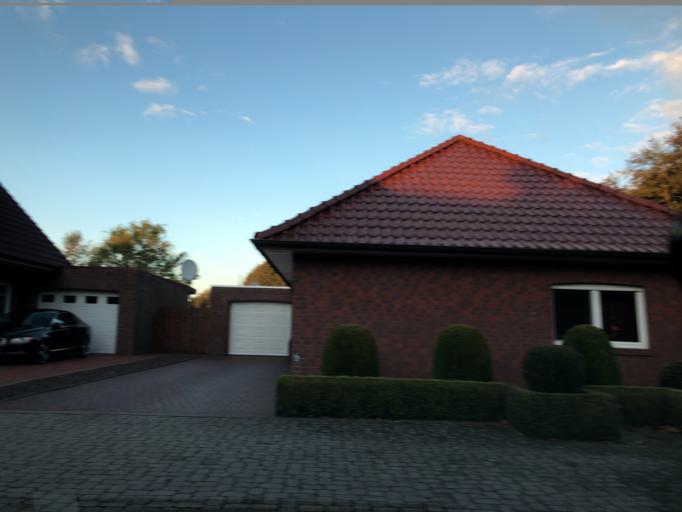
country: DE
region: Lower Saxony
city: Papenburg
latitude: 53.0868
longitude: 7.4216
